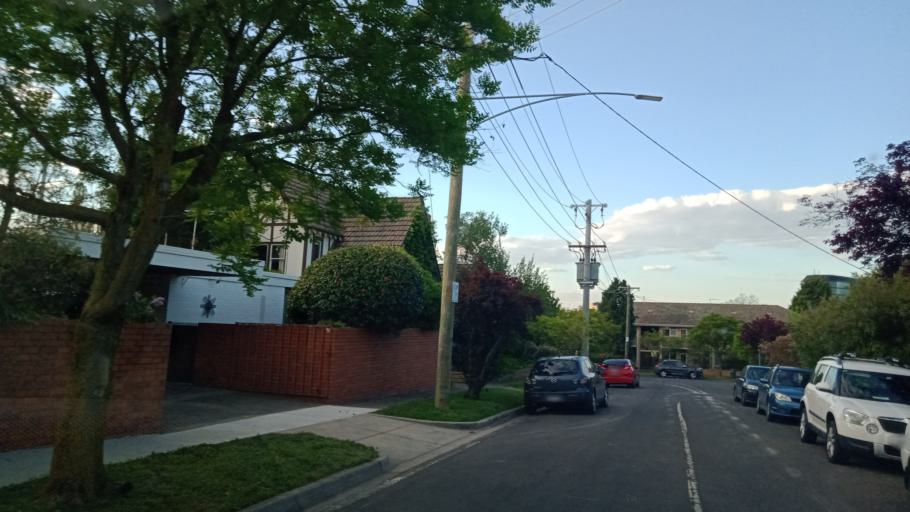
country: AU
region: Victoria
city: Glenferrie
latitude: -37.8350
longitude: 145.0545
